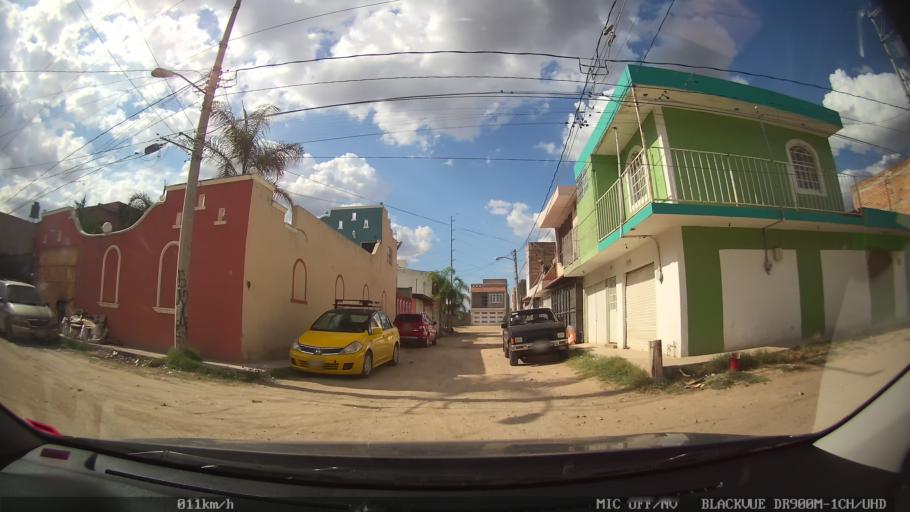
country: MX
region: Jalisco
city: Tlaquepaque
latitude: 20.6628
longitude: -103.2656
